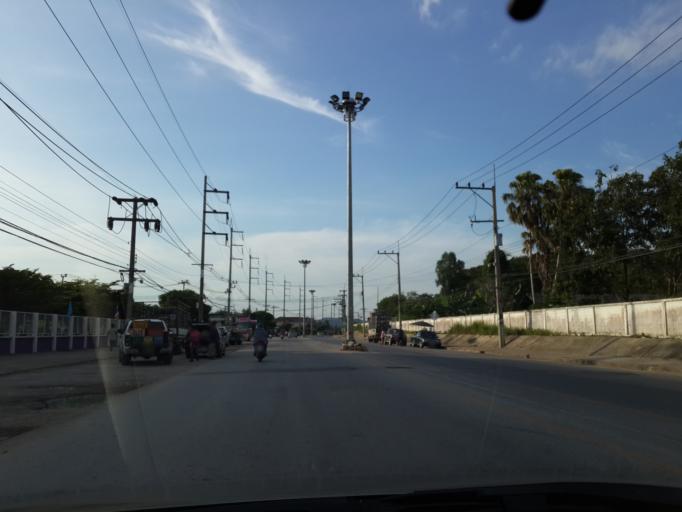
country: TH
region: Yala
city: Yala
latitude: 6.5150
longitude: 101.2715
